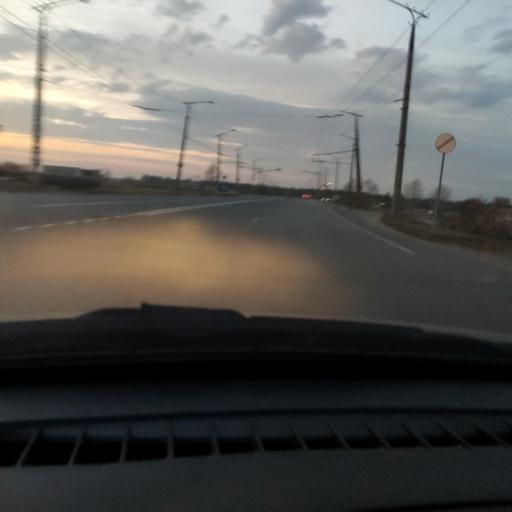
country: RU
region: Samara
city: Povolzhskiy
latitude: 53.5451
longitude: 49.6048
